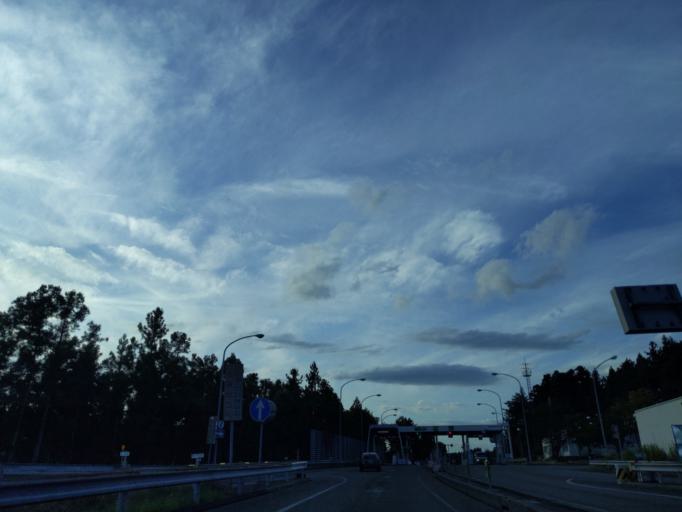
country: JP
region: Niigata
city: Kashiwazaki
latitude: 37.4417
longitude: 138.6577
